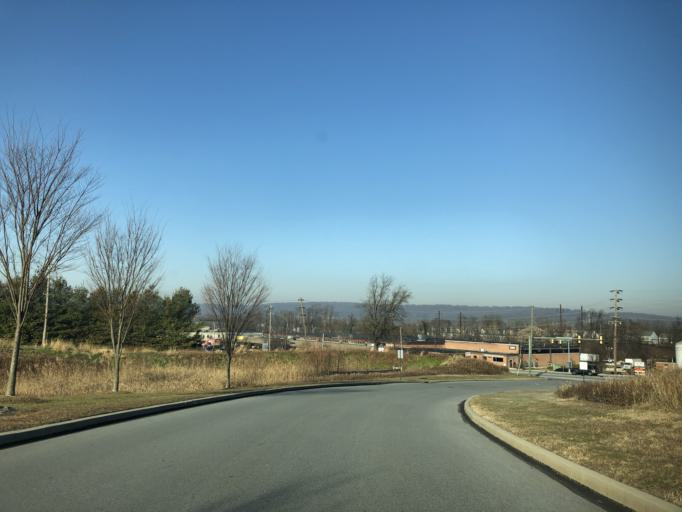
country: US
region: Pennsylvania
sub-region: Chester County
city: Downingtown
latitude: 40.0009
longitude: -75.6934
